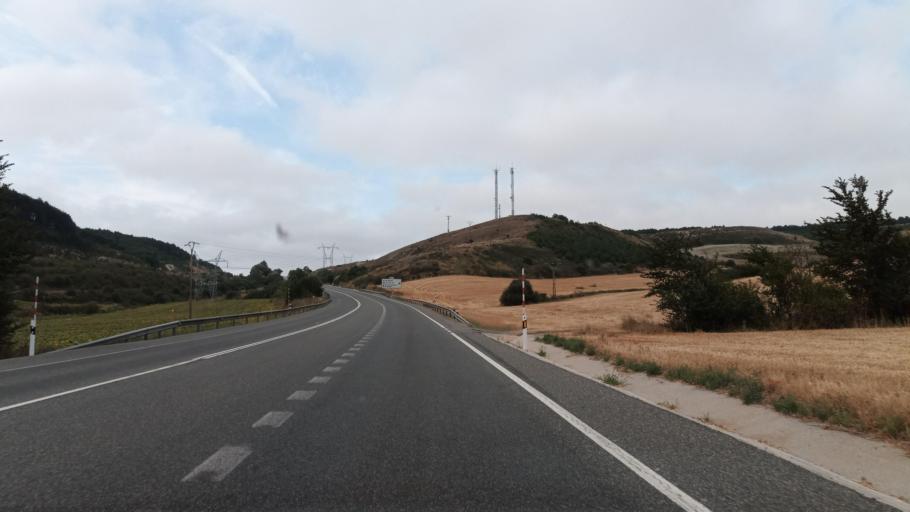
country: ES
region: Castille and Leon
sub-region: Provincia de Burgos
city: Monasterio de Rodilla
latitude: 42.4497
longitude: -3.4831
